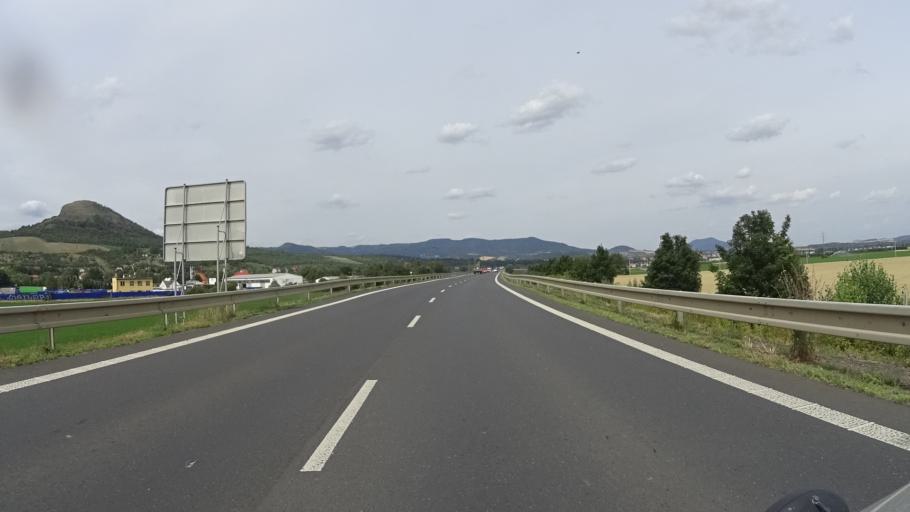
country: CZ
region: Ustecky
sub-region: Okres Litomerice
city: Litomerice
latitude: 50.5146
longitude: 14.0978
